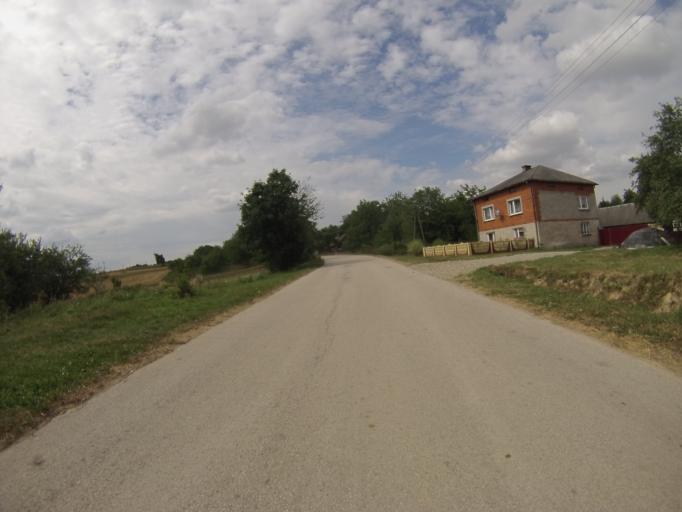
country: PL
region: Swietokrzyskie
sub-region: Powiat kielecki
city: Lagow
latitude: 50.7414
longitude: 21.1215
